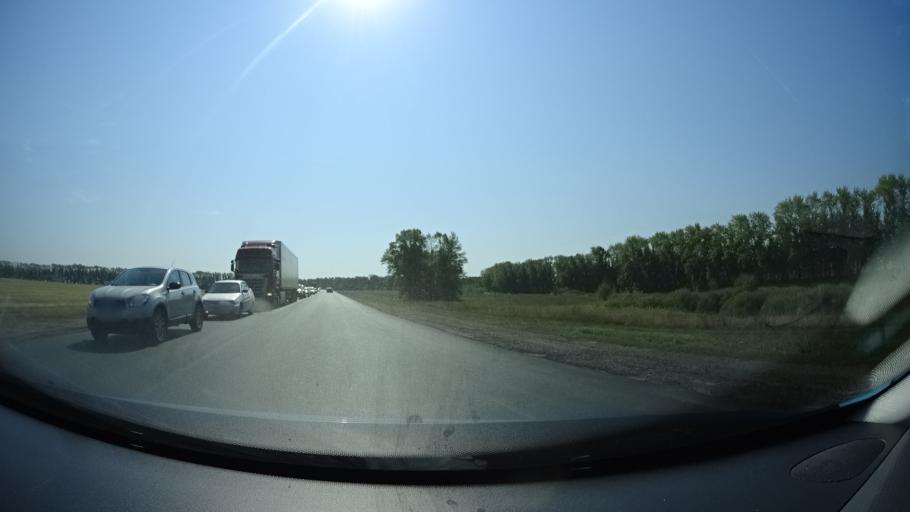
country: RU
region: Bashkortostan
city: Kabakovo
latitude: 54.4845
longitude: 55.9217
